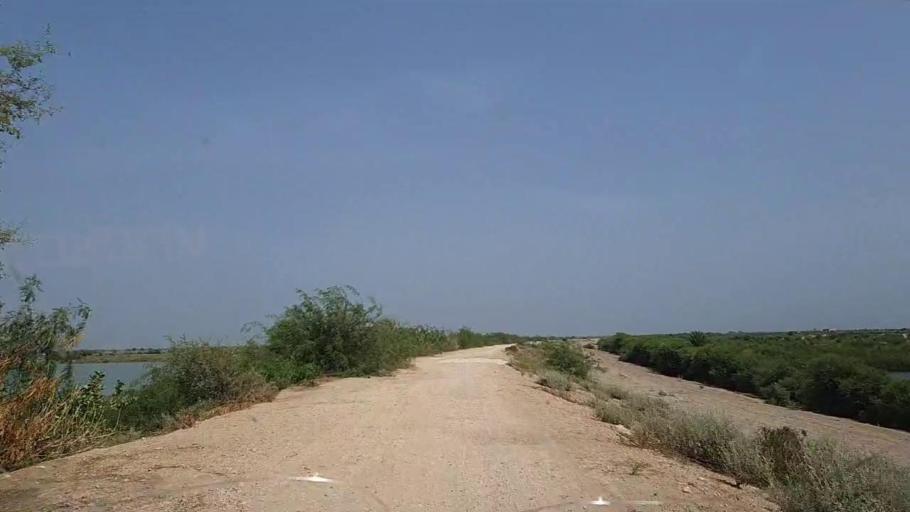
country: PK
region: Sindh
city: Ghotki
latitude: 28.1141
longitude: 69.3887
